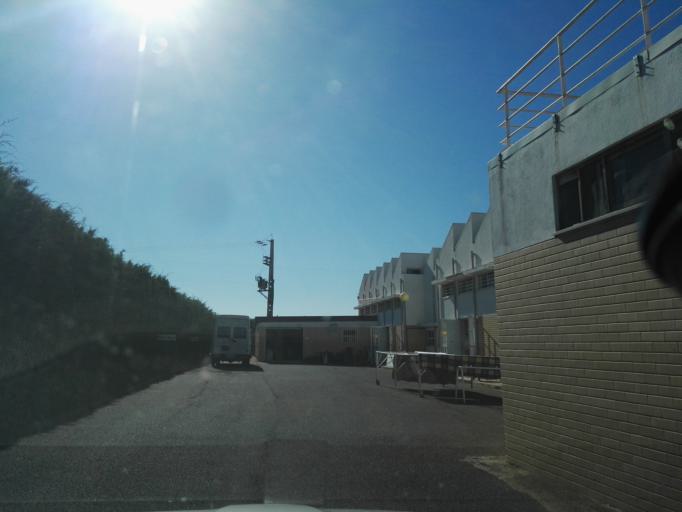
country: PT
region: Portalegre
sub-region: Elvas
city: Elvas
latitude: 38.8692
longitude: -7.1598
